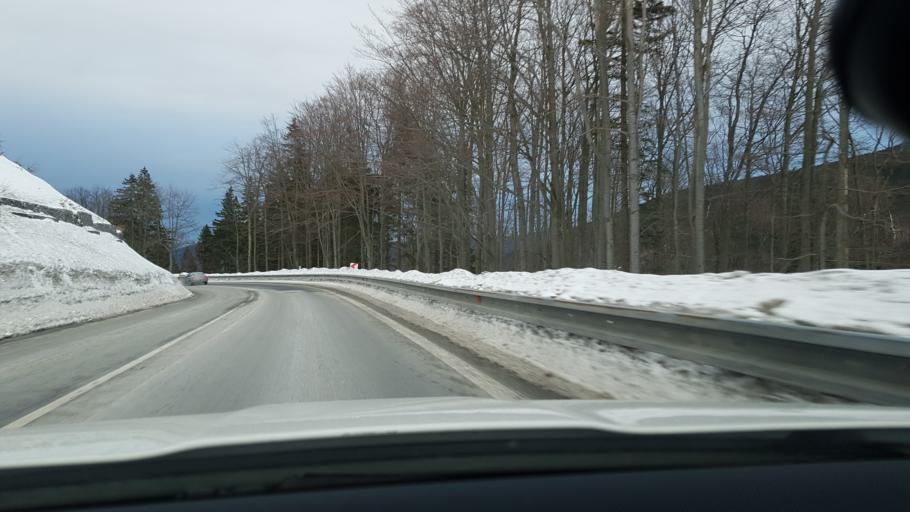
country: CZ
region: Olomoucky
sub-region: Okres Sumperk
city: Loucna nad Desnou
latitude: 50.1310
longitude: 17.1567
